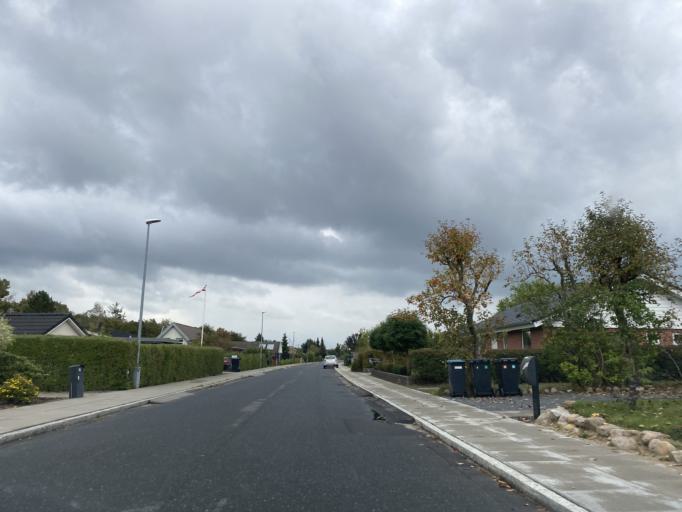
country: DK
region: Central Jutland
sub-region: Silkeborg Kommune
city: Svejbaek
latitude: 56.1746
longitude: 9.6204
